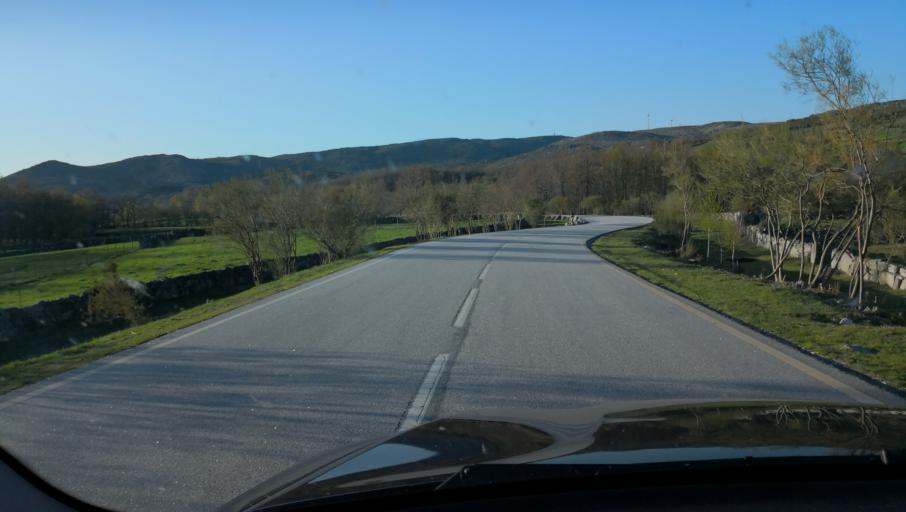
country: PT
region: Vila Real
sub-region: Vila Real
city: Vila Real
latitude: 41.3661
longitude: -7.8008
